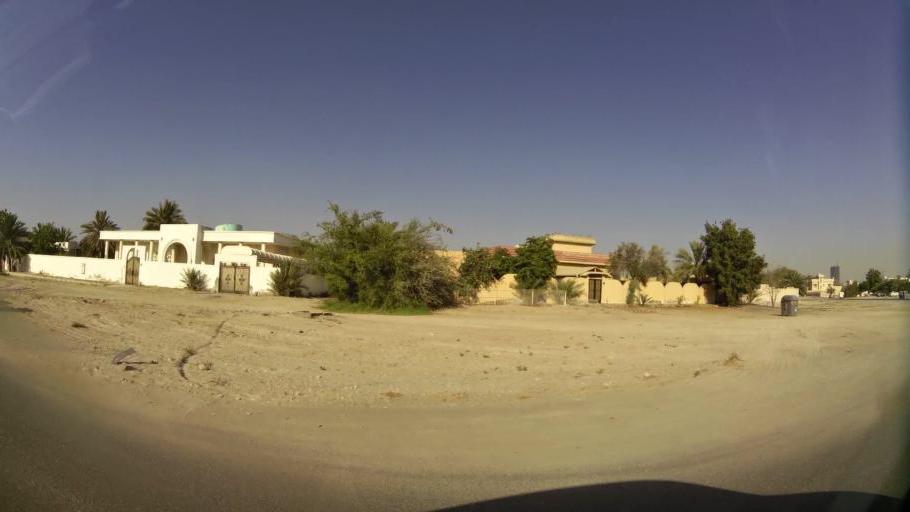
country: AE
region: Ajman
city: Ajman
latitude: 25.4059
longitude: 55.4629
